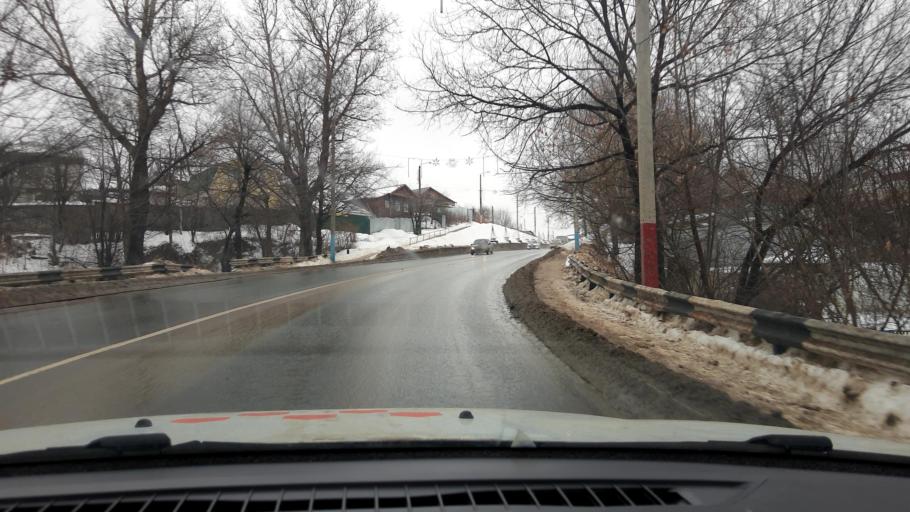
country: RU
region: Nizjnij Novgorod
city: Pavlovo
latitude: 55.9672
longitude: 43.0747
